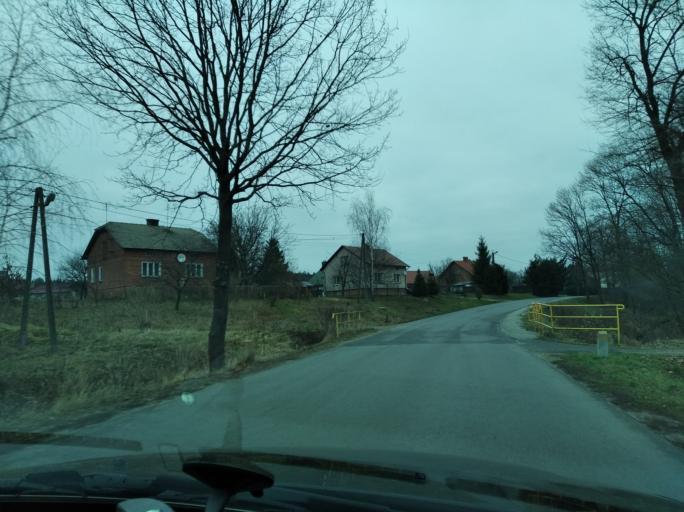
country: PL
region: Subcarpathian Voivodeship
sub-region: Powiat lancucki
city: Rakszawa
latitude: 50.1648
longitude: 22.1980
